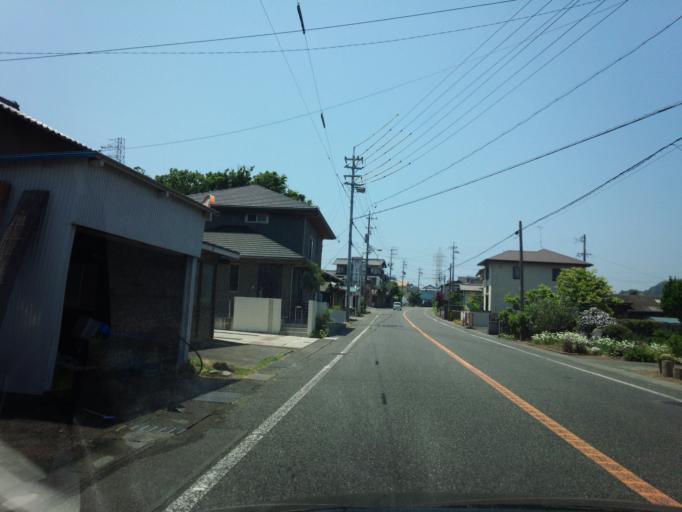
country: JP
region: Shizuoka
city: Shizuoka-shi
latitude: 34.9780
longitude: 138.5006
